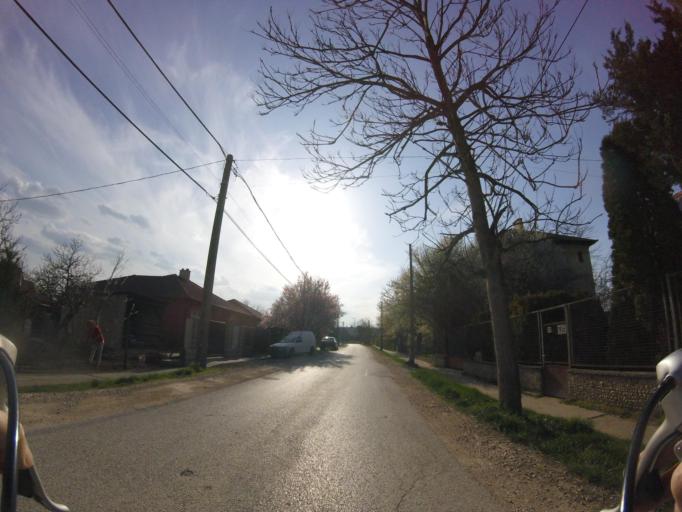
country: HU
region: Pest
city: Diosd
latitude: 47.3897
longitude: 18.9388
